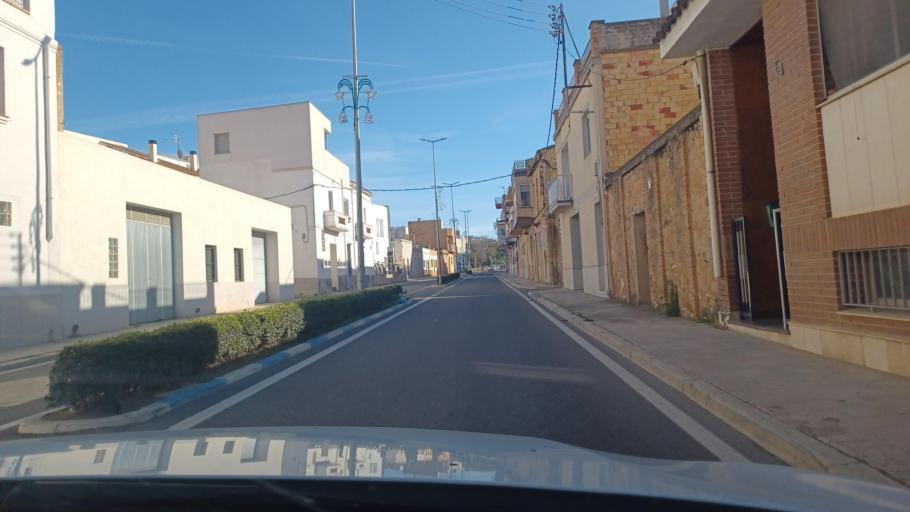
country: ES
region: Catalonia
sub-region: Provincia de Tarragona
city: Masdenverge
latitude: 40.7141
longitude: 0.5311
